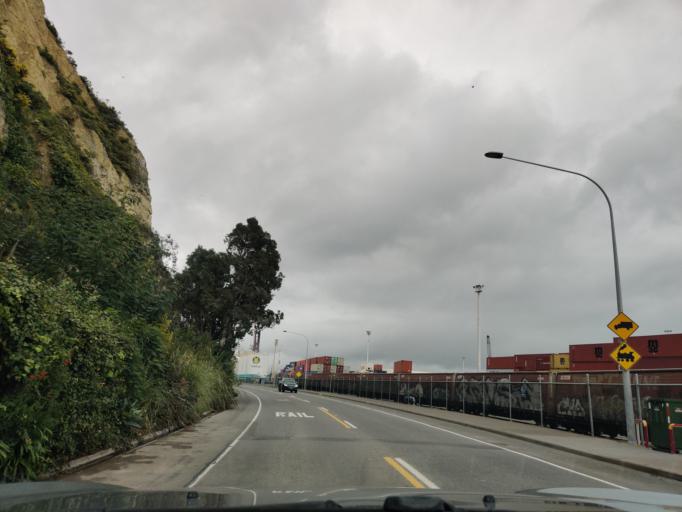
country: NZ
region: Hawke's Bay
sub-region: Napier City
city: Napier
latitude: -39.4778
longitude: 176.9172
